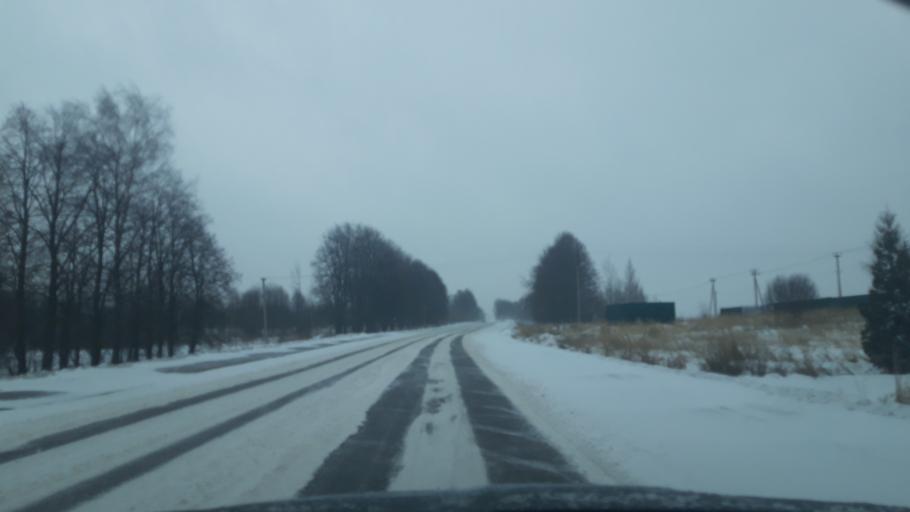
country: RU
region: Moskovskaya
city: Yakhroma
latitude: 56.3013
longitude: 37.4570
